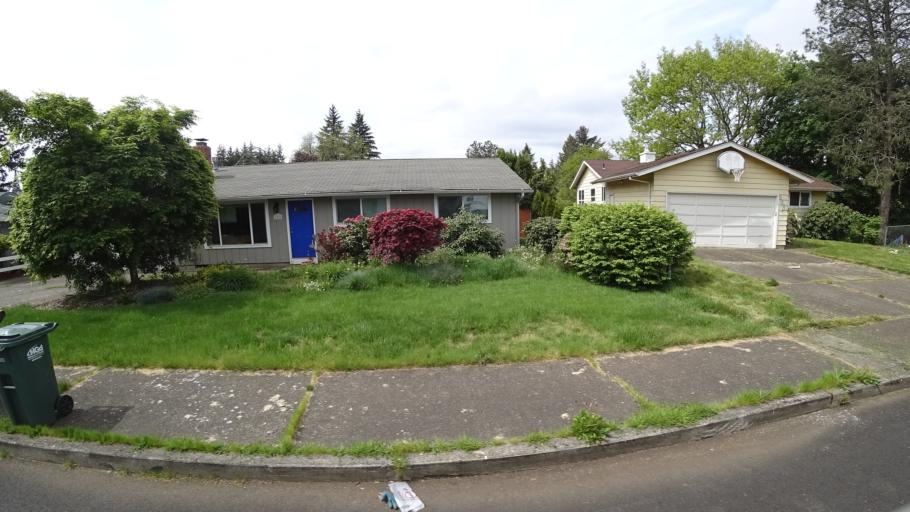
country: US
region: Oregon
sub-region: Washington County
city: Hillsboro
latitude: 45.5304
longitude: -122.9922
